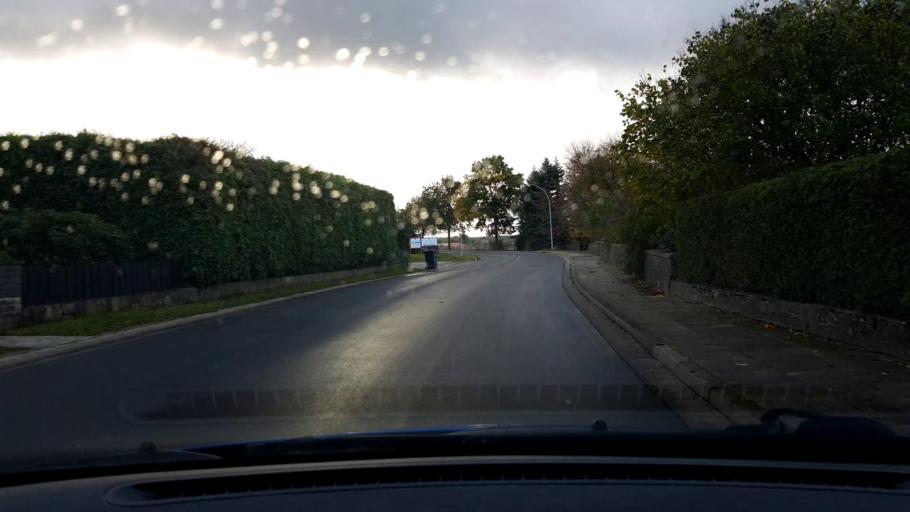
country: DE
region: Lower Saxony
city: Reinstorf
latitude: 53.2404
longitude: 10.5829
